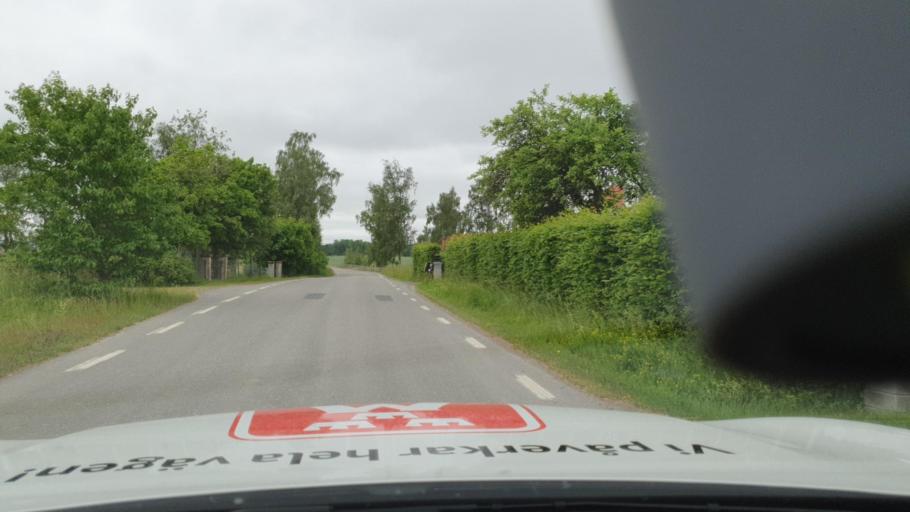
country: SE
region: Vaestra Goetaland
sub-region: Tibro Kommun
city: Tibro
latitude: 58.3953
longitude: 14.1166
